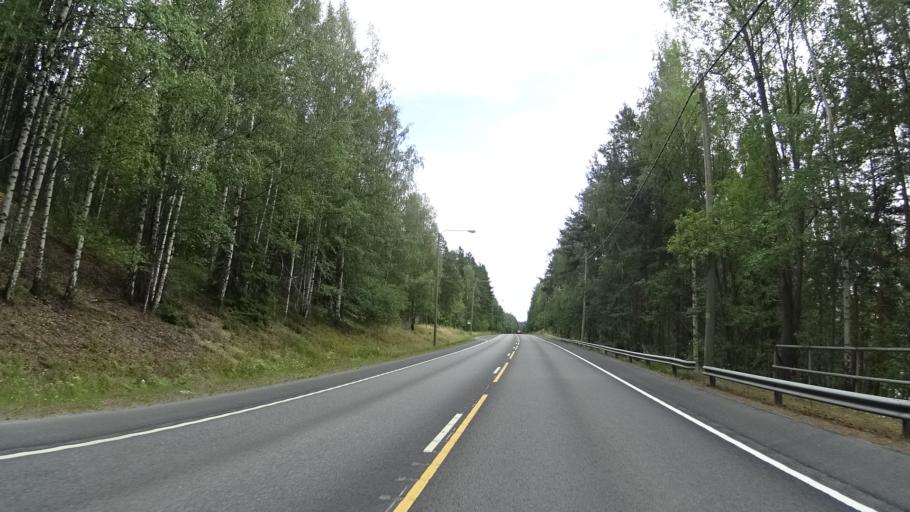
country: FI
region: Pirkanmaa
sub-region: Tampere
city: Kangasala
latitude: 61.4298
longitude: 24.1302
